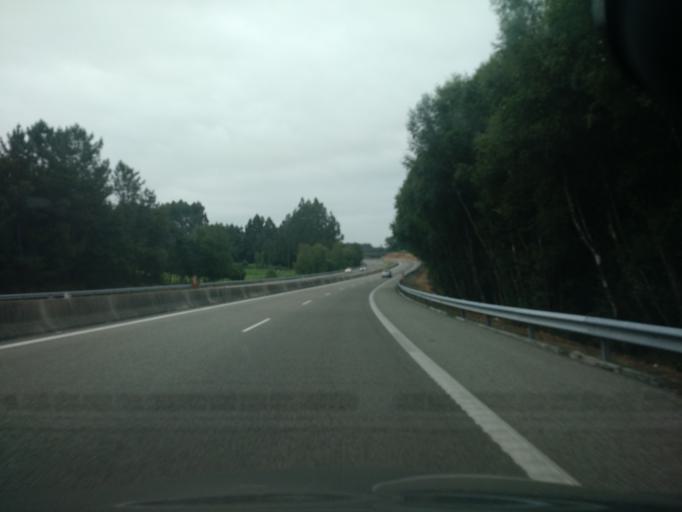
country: ES
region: Galicia
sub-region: Provincia da Coruna
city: Ordes
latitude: 43.0562
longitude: -8.3713
